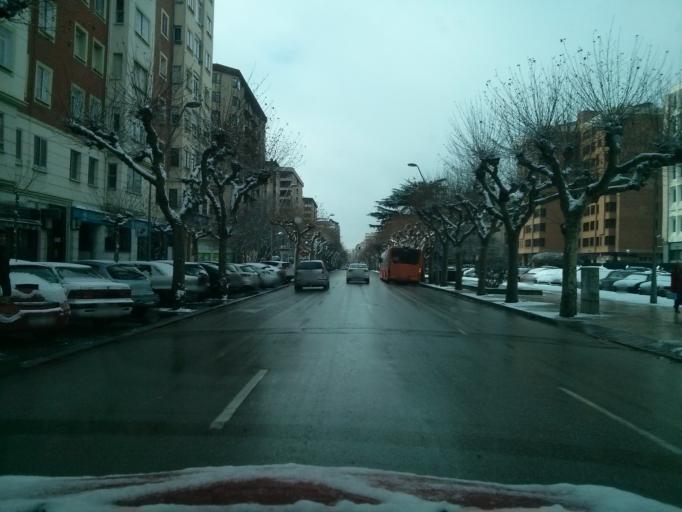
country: ES
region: Castille and Leon
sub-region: Provincia de Burgos
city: Burgos
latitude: 42.3435
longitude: -3.6883
